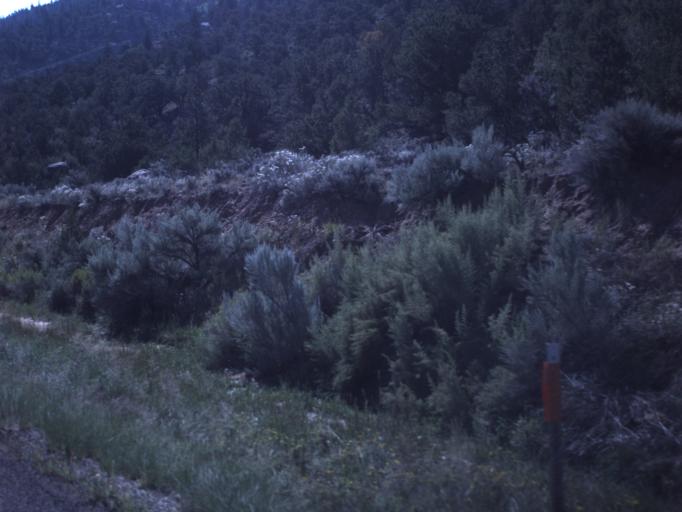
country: US
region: Utah
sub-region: Duchesne County
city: Duchesne
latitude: 40.2966
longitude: -110.5787
